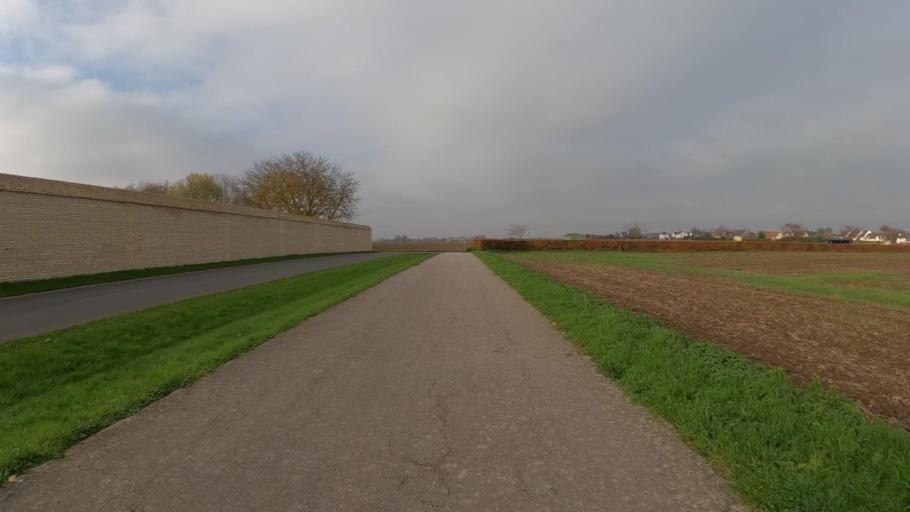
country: FR
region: Lower Normandy
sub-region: Departement du Calvados
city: Saint-Germain-la-Blanche-Herbe
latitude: 49.1973
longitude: -0.4134
